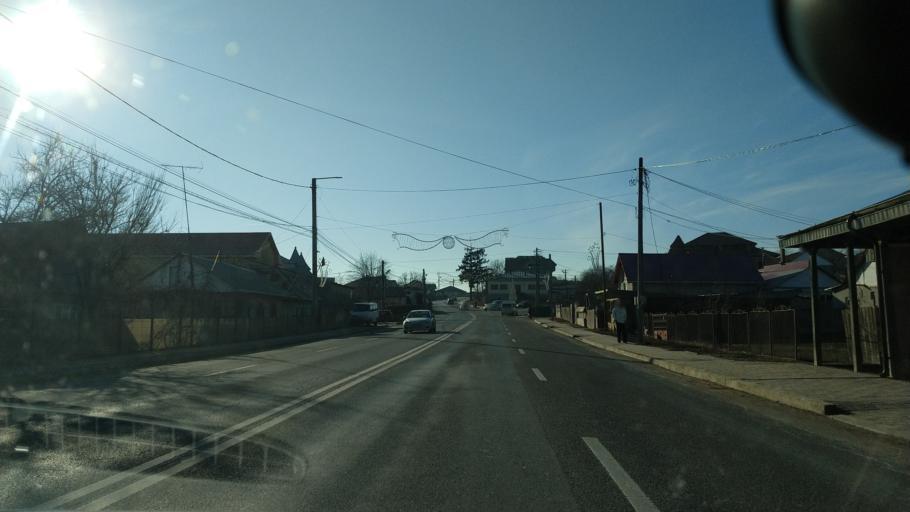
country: RO
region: Iasi
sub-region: Comuna Targu Frumos
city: Targu Frumos
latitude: 47.2051
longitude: 27.0087
